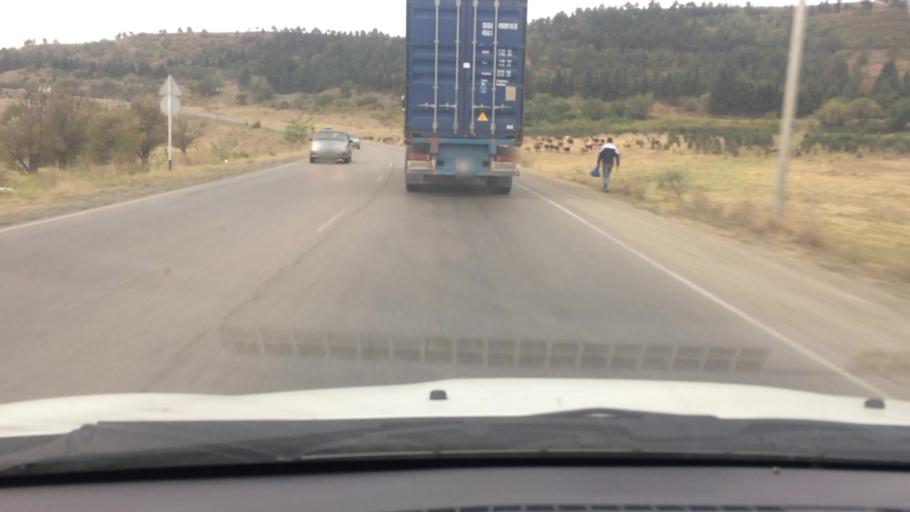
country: GE
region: T'bilisi
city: Tbilisi
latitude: 41.6030
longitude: 44.7795
